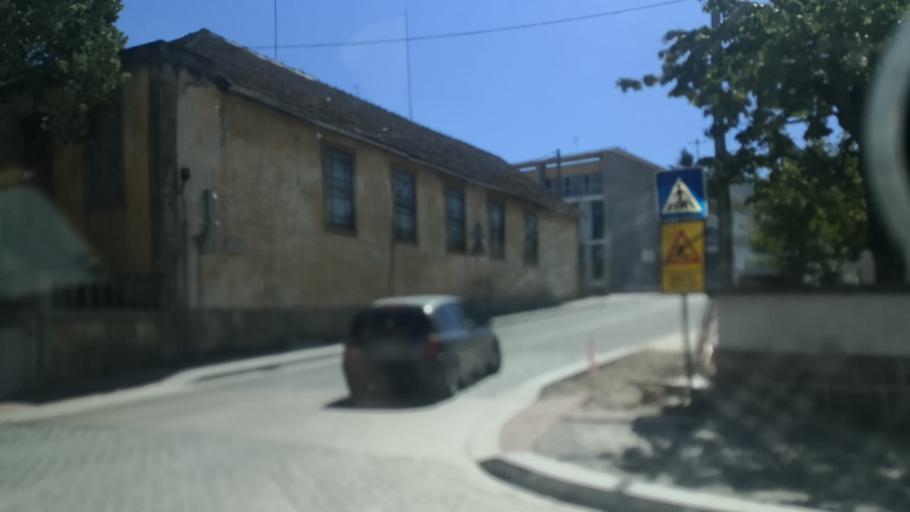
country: PT
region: Braganca
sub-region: Braganca Municipality
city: Braganca
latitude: 41.8086
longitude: -6.7597
